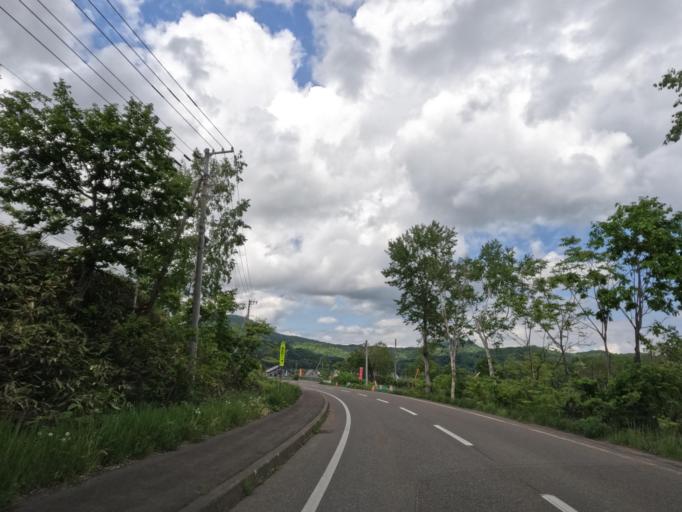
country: JP
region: Hokkaido
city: Takikawa
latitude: 43.5849
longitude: 141.7314
